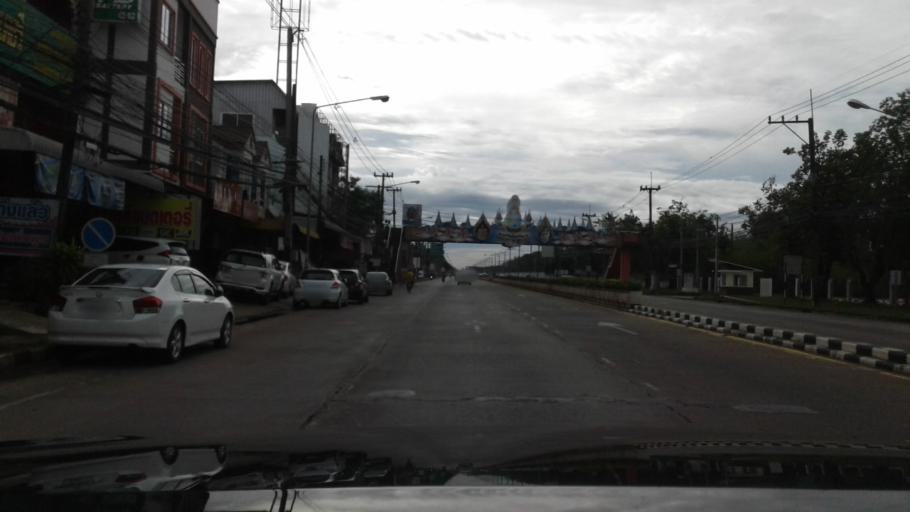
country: TH
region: Changwat Udon Thani
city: Udon Thani
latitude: 17.3873
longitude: 102.8022
